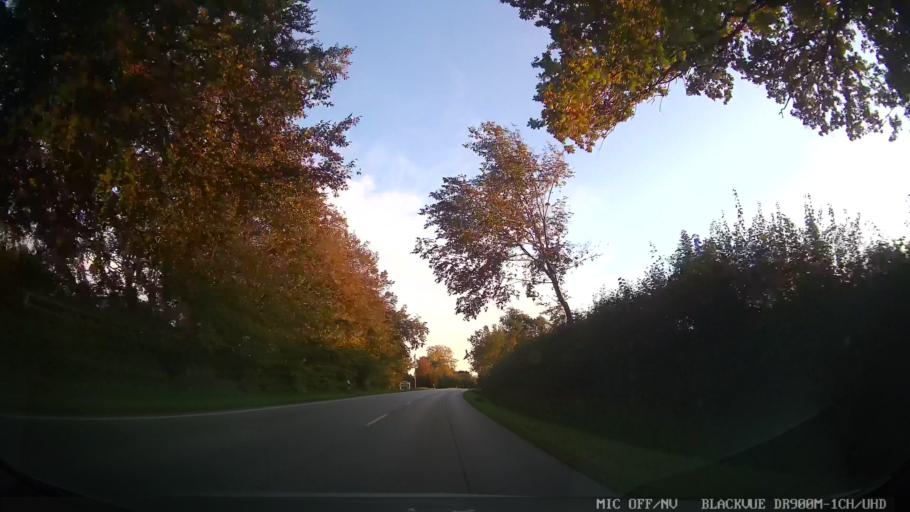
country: DE
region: Schleswig-Holstein
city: Susel
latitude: 54.0690
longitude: 10.6876
